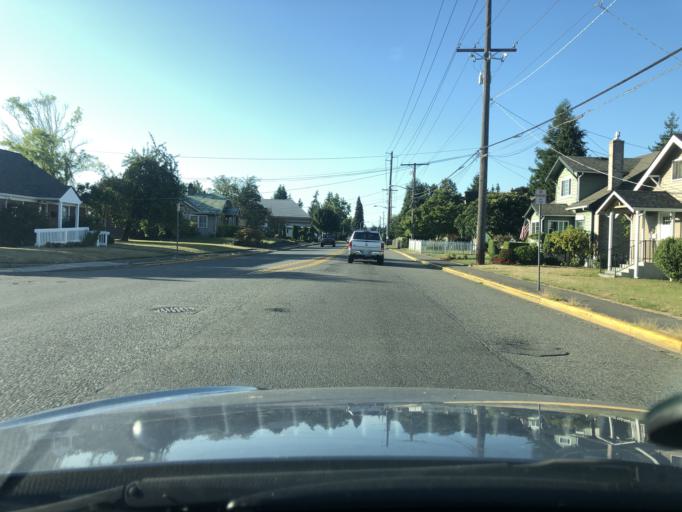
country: US
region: Washington
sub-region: King County
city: Auburn
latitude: 47.3087
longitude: -122.2134
